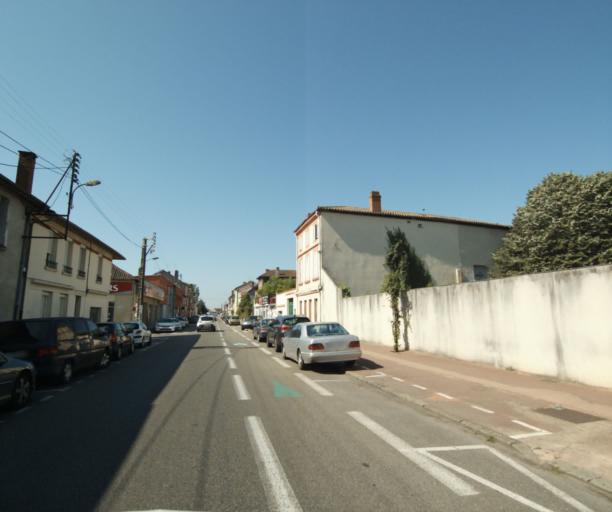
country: FR
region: Midi-Pyrenees
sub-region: Departement du Tarn-et-Garonne
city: Montauban
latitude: 44.0091
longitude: 1.3440
